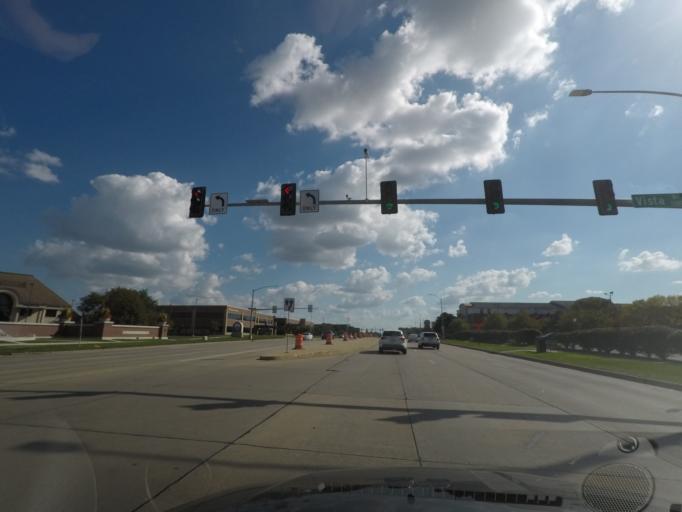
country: US
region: Iowa
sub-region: Dallas County
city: Waukee
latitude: 41.5891
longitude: -93.8092
